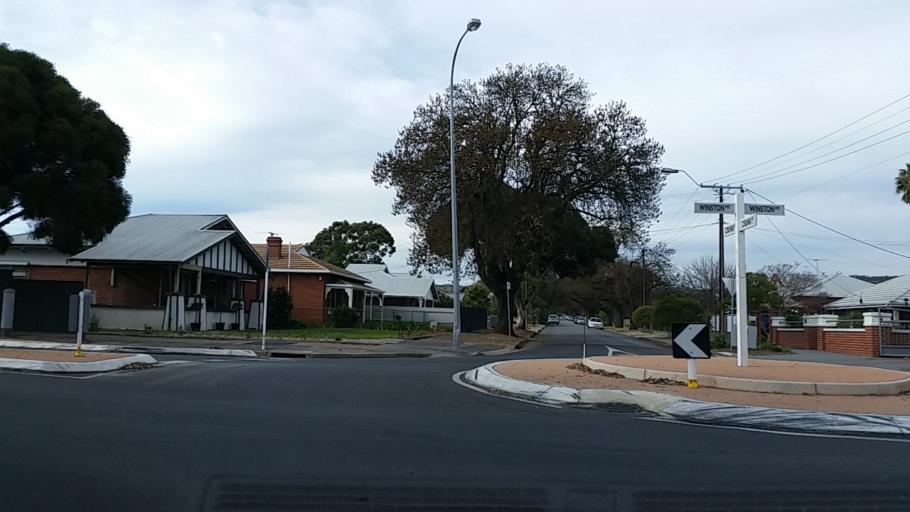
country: AU
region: South Australia
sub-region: Mitcham
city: Clarence Gardens
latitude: -34.9845
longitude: 138.5829
